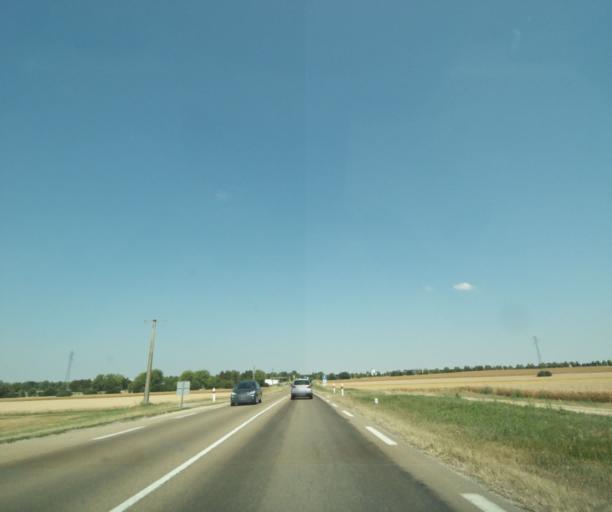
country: FR
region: Champagne-Ardenne
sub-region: Departement de la Marne
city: Sarry
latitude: 48.9330
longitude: 4.4044
